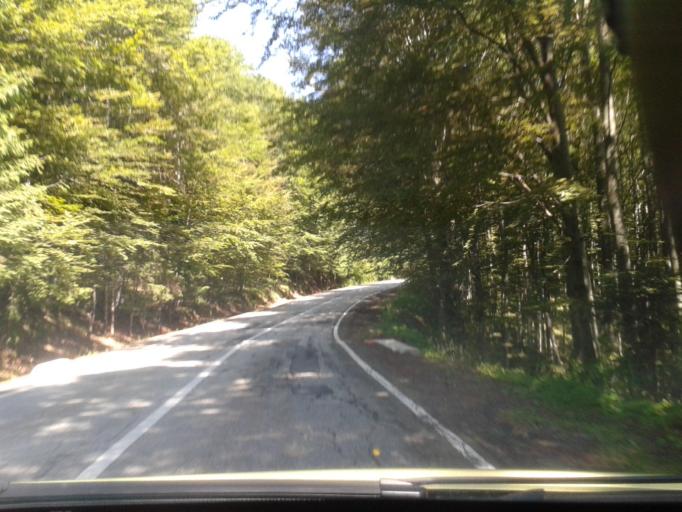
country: RO
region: Sibiu
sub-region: Comuna Cartisoara
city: Cartisoara
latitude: 45.6767
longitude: 24.5857
